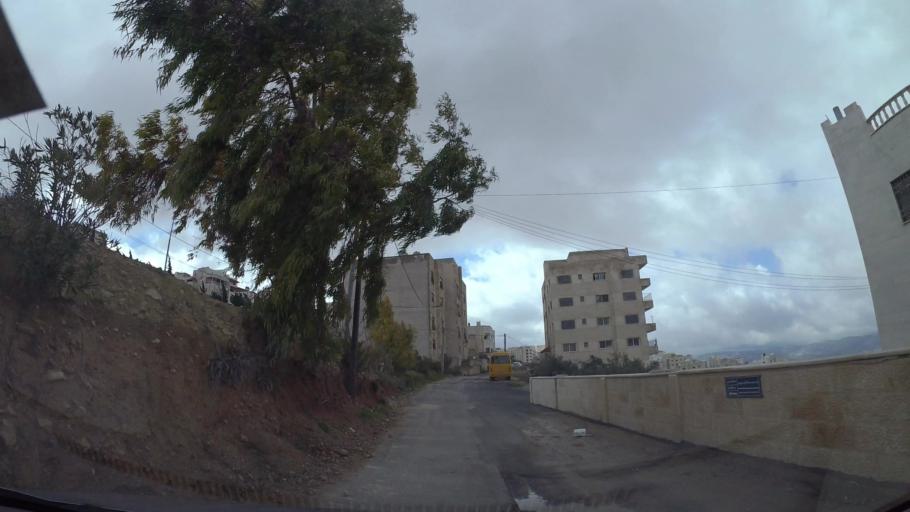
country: JO
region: Amman
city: Al Jubayhah
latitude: 32.0688
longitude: 35.8781
